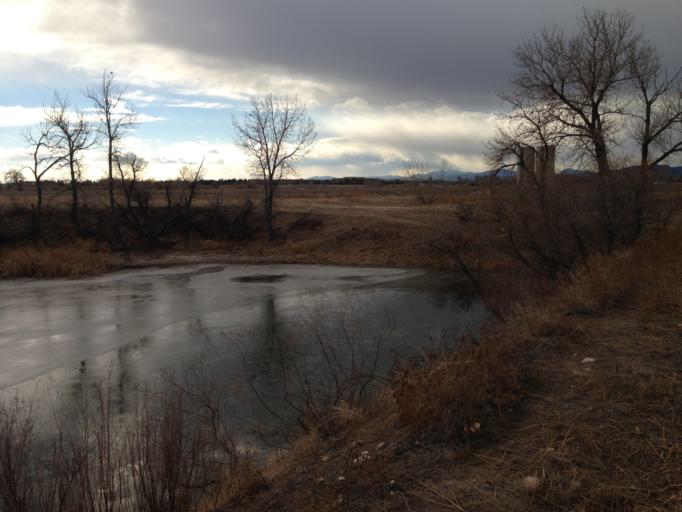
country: US
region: Colorado
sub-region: Larimer County
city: Fort Collins
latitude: 40.5365
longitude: -105.0003
